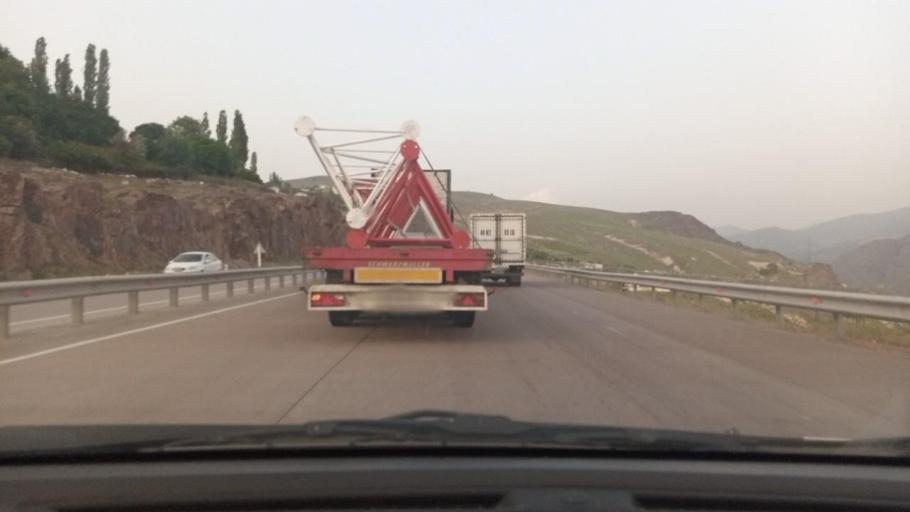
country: UZ
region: Toshkent
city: Angren
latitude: 41.0734
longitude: 70.2574
